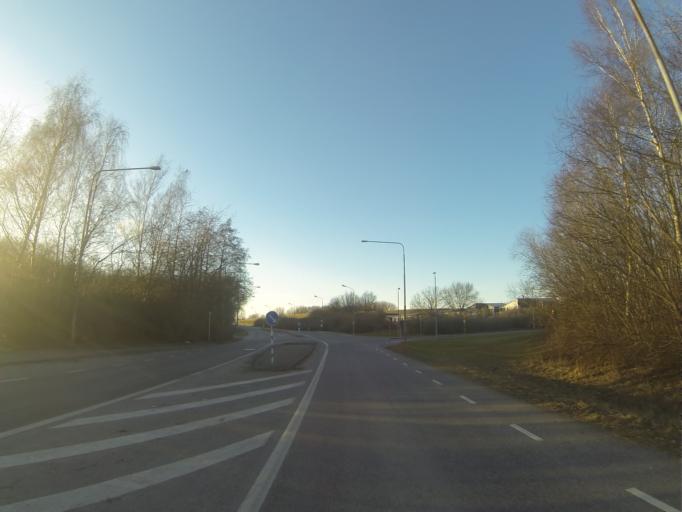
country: SE
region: Skane
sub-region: Malmo
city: Oxie
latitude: 55.5437
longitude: 13.0918
